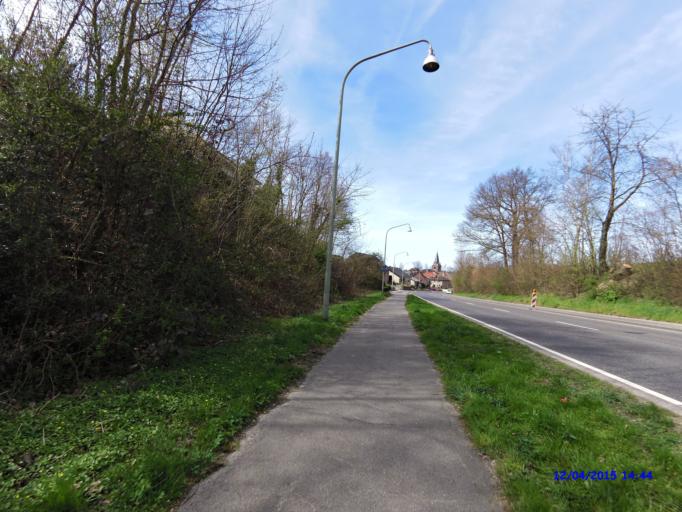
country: DE
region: North Rhine-Westphalia
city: Geilenkirchen
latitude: 50.9785
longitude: 6.0793
